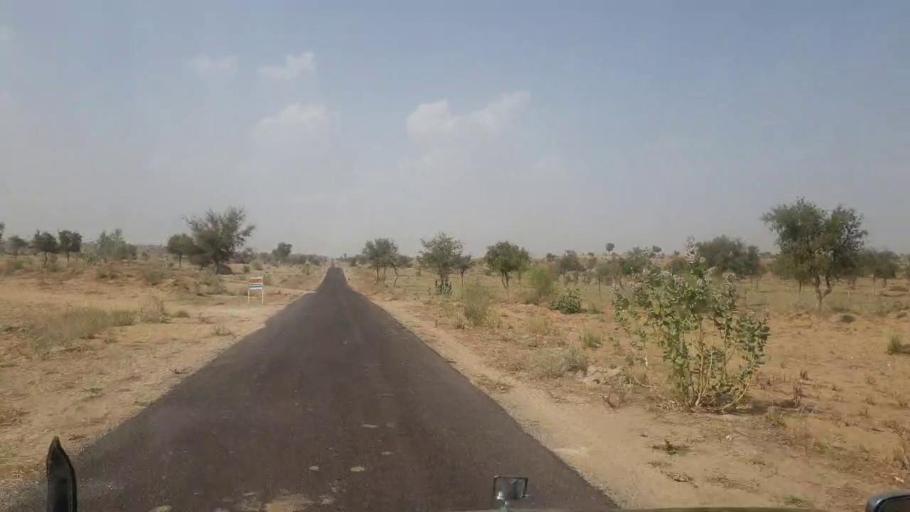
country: PK
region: Sindh
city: Islamkot
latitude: 25.1841
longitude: 70.2865
